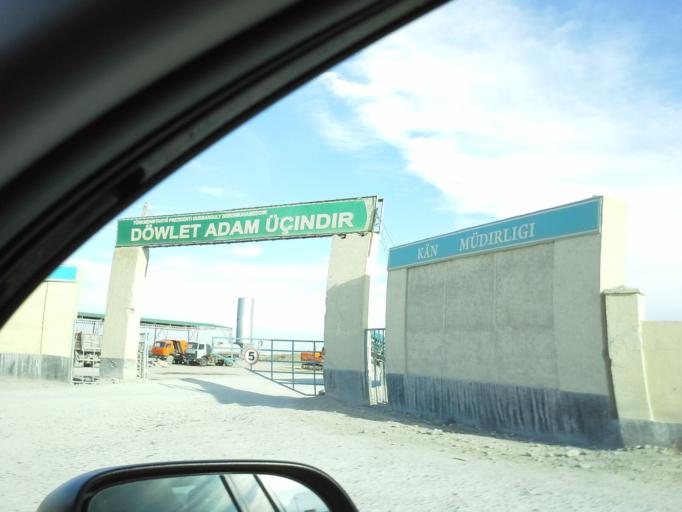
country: TM
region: Ahal
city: Abadan
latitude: 38.0388
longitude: 58.1617
